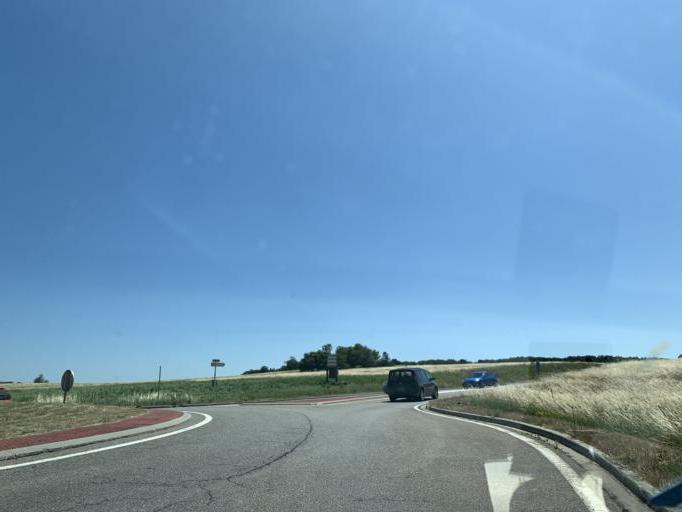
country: FR
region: Provence-Alpes-Cote d'Azur
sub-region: Departement des Hautes-Alpes
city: Gap
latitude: 44.6147
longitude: 6.1375
